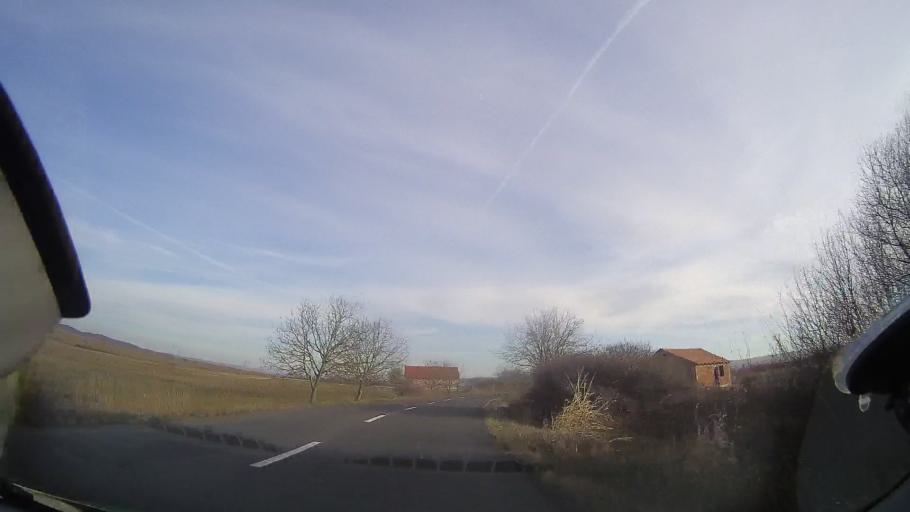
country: RO
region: Bihor
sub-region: Comuna Tileagd
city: Tileagd
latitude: 47.0652
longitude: 22.2221
